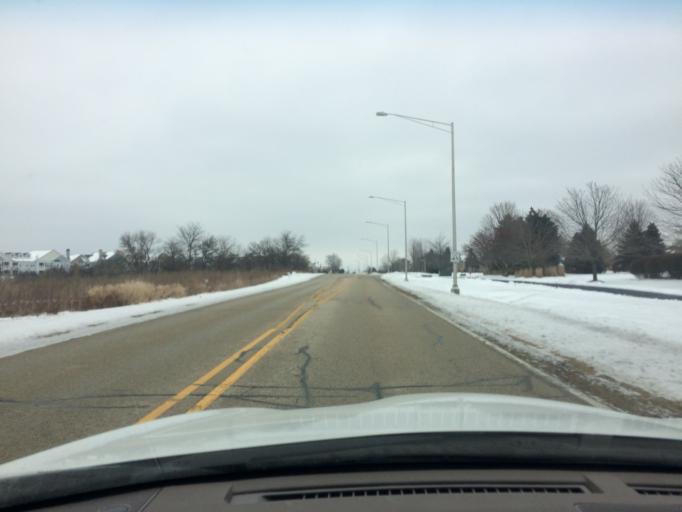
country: US
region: Illinois
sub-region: Kane County
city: Saint Charles
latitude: 41.8976
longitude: -88.3515
